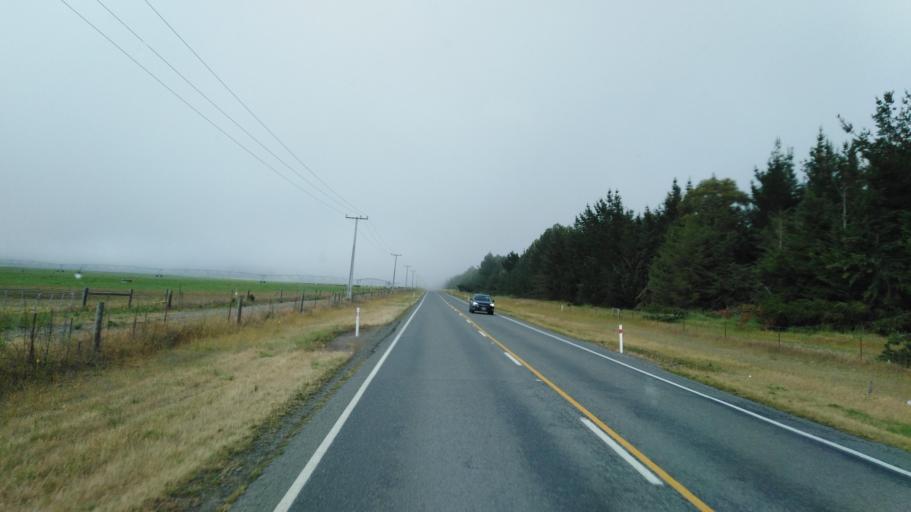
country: NZ
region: Canterbury
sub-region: Hurunui District
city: Amberley
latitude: -42.8190
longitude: 172.8122
